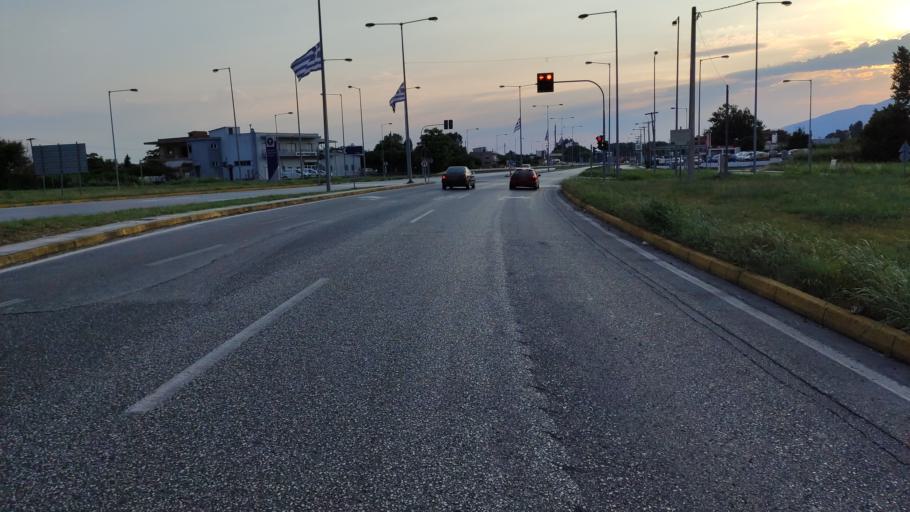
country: GR
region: East Macedonia and Thrace
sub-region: Nomos Rodopis
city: Komotini
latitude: 41.1137
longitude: 25.3871
